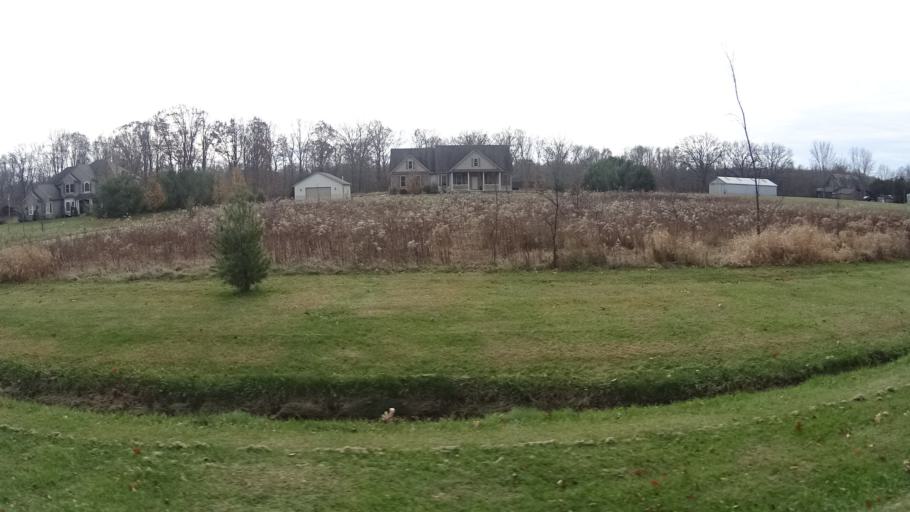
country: US
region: Ohio
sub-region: Lorain County
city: Eaton Estates
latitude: 41.2748
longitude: -81.9375
